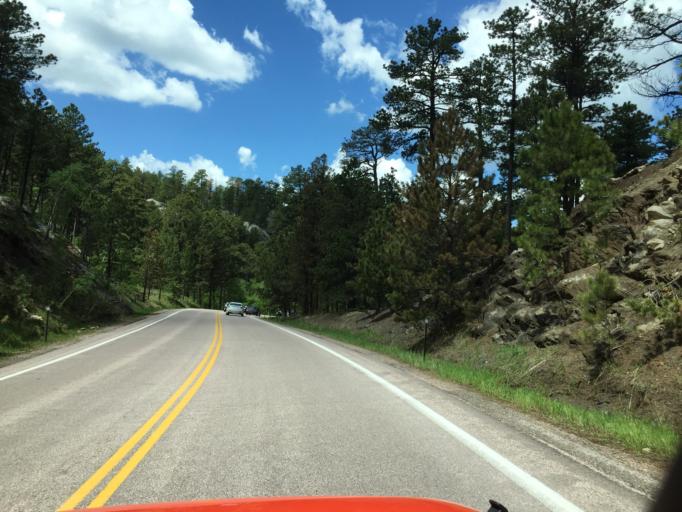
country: US
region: South Dakota
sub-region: Custer County
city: Custer
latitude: 43.8840
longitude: -103.4649
